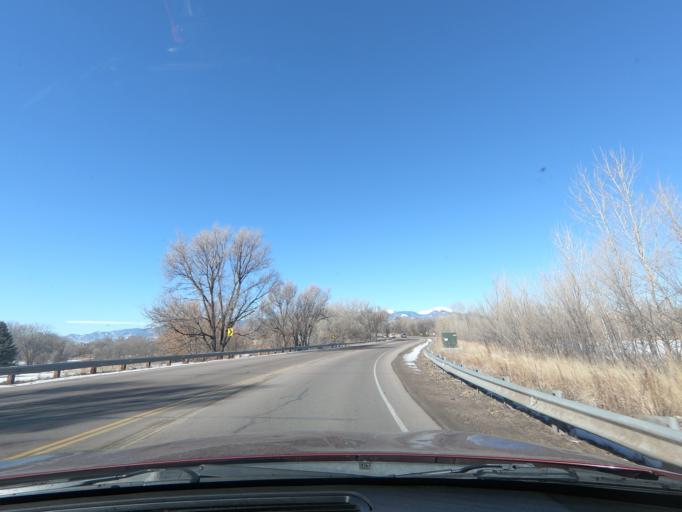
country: US
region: Colorado
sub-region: El Paso County
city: Security-Widefield
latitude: 38.7369
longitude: -104.7101
